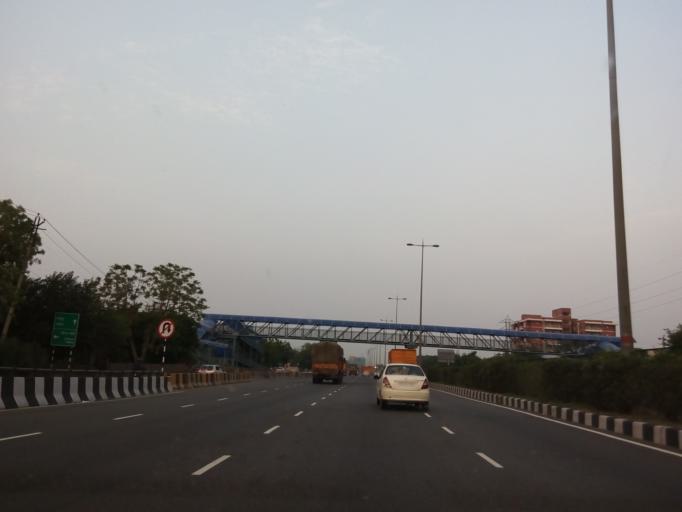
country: IN
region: Haryana
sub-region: Gurgaon
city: Gurgaon
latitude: 28.4734
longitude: 77.0634
